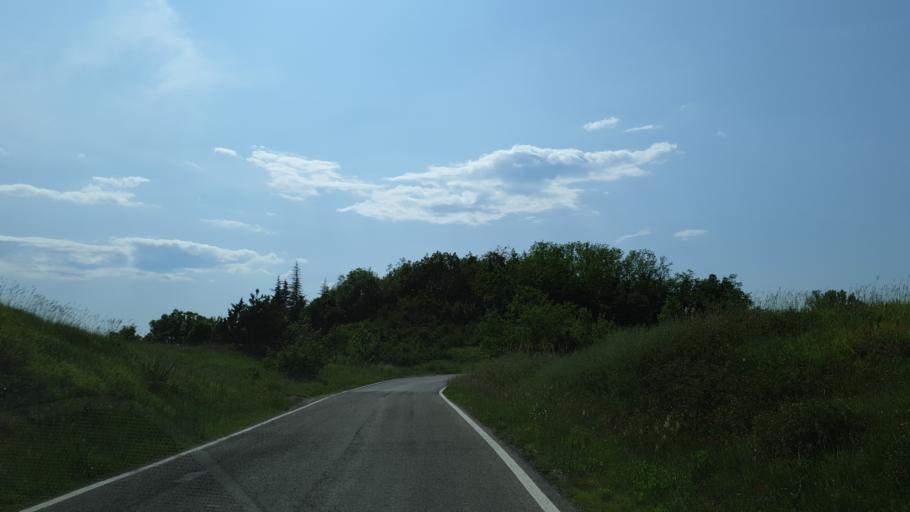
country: IT
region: Emilia-Romagna
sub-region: Provincia di Rimini
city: Sant'Agata Feltria
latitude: 43.9089
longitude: 12.2147
